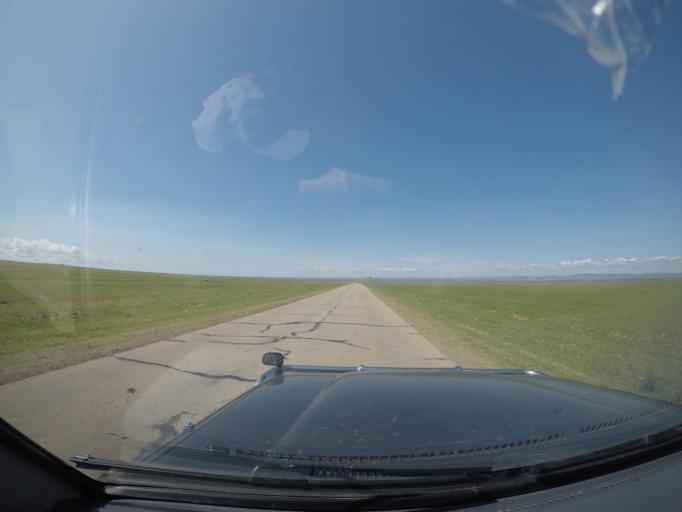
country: MN
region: Hentiy
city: Undurkhaan
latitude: 47.2793
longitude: 110.7622
